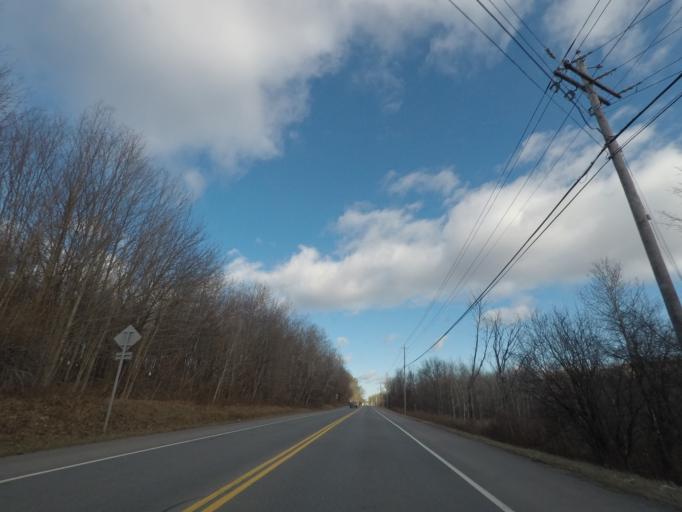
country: US
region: New York
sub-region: Saratoga County
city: Waterford
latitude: 42.7669
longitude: -73.6611
